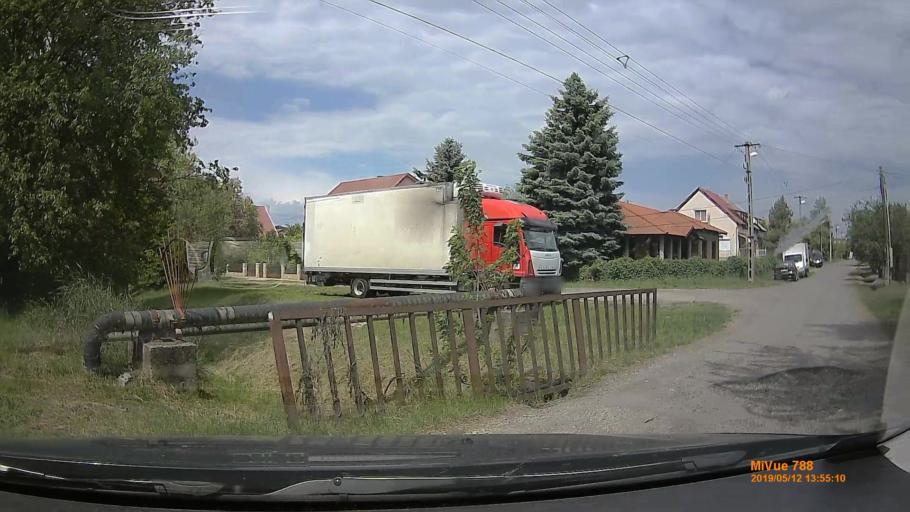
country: HU
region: Pest
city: Pecel
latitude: 47.4890
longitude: 19.2975
